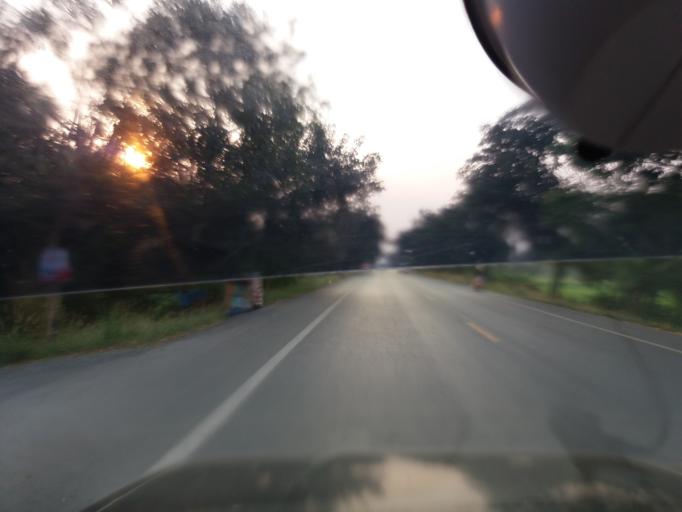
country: TH
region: Sing Buri
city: Bang Racham
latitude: 14.8831
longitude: 100.3482
